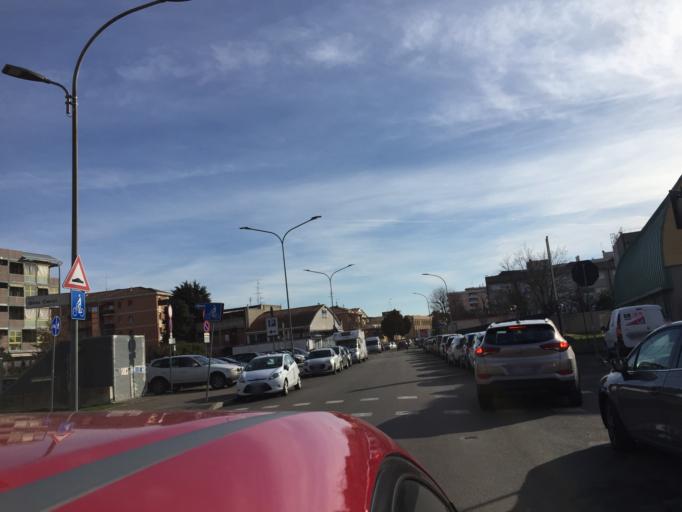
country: IT
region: Emilia-Romagna
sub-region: Provincia di Bologna
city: Bologna
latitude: 44.5037
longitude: 11.3033
